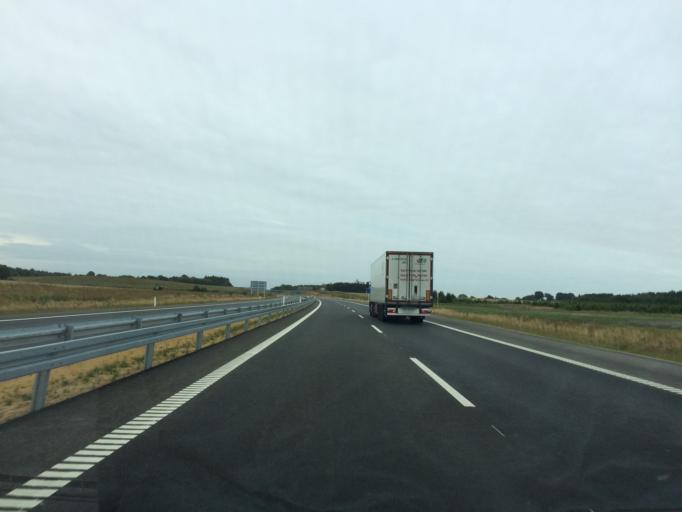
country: DK
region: Central Jutland
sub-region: Herning Kommune
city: Snejbjerg
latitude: 56.1424
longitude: 8.8694
